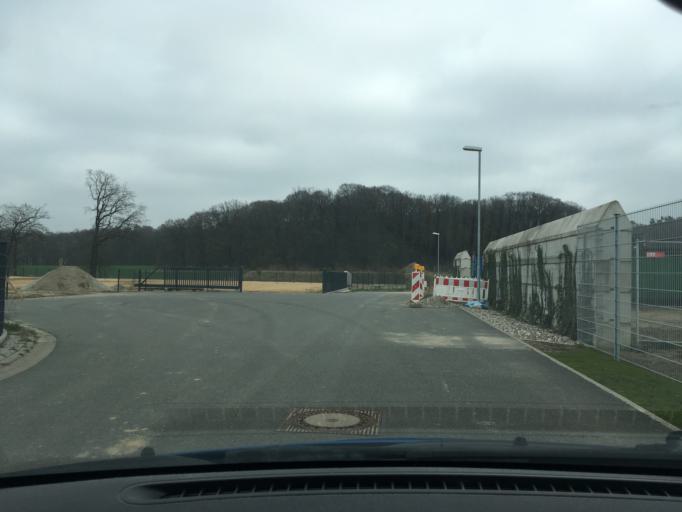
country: DE
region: Lower Saxony
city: Sudergellersen
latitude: 53.2249
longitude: 10.2868
